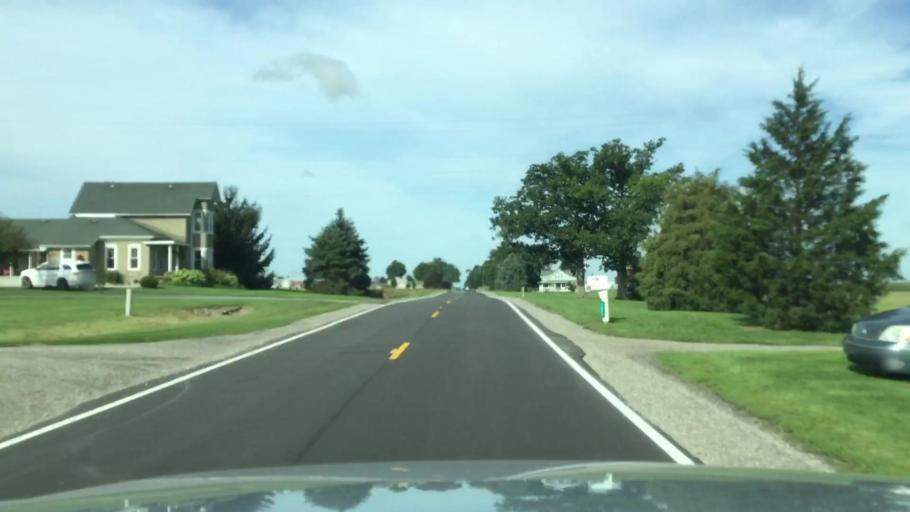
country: US
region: Michigan
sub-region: Genesee County
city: Montrose
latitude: 43.1471
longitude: -83.9418
